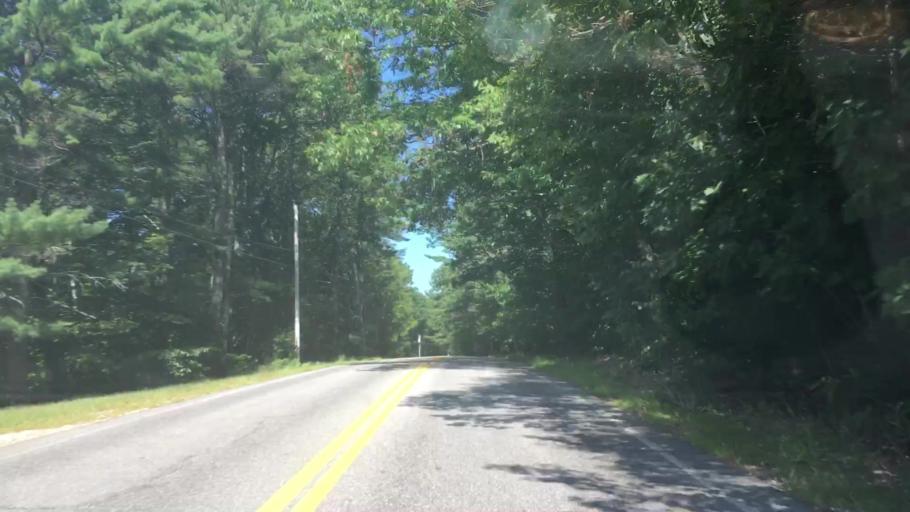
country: US
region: Maine
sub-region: Androscoggin County
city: Lisbon
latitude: 44.0586
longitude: -70.1180
